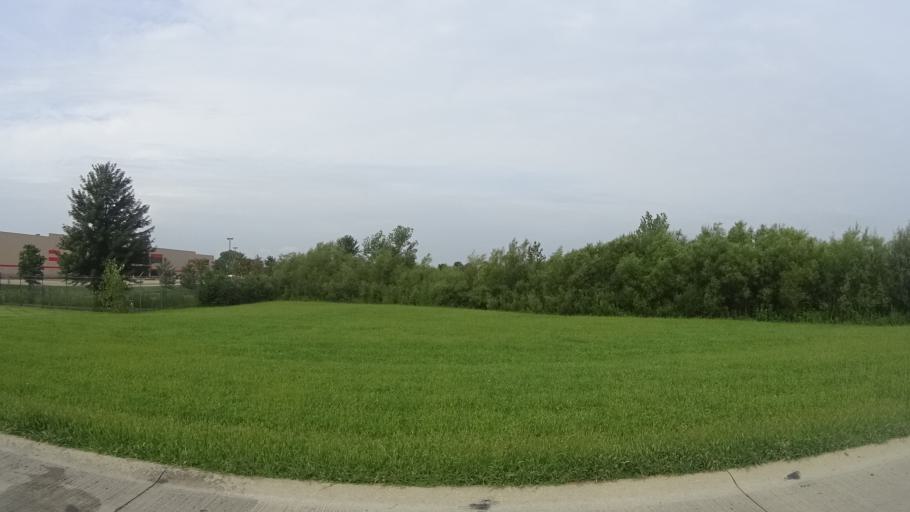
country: US
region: Indiana
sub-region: Madison County
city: Pendleton
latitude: 40.0012
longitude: -85.7711
